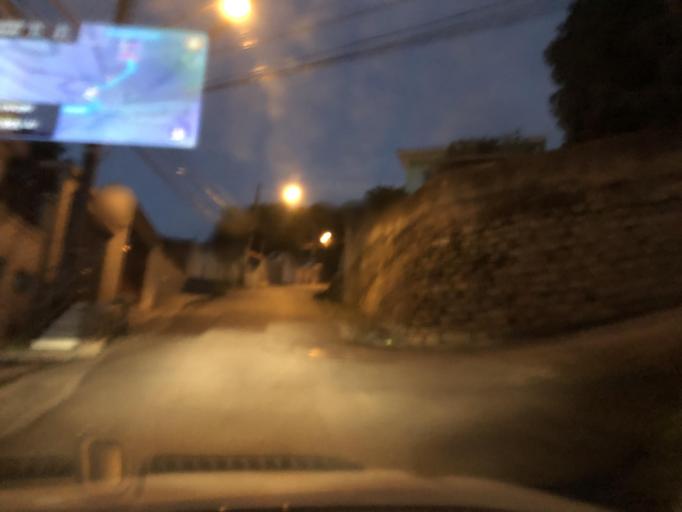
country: BR
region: Santa Catarina
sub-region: Florianopolis
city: Morro da Cruz
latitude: -27.5844
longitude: -48.5396
